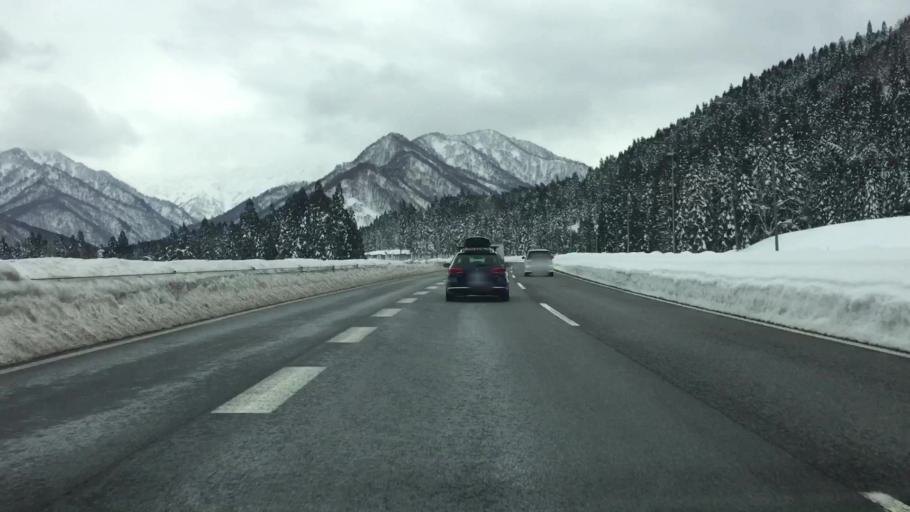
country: JP
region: Niigata
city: Shiozawa
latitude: 36.8900
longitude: 138.8481
